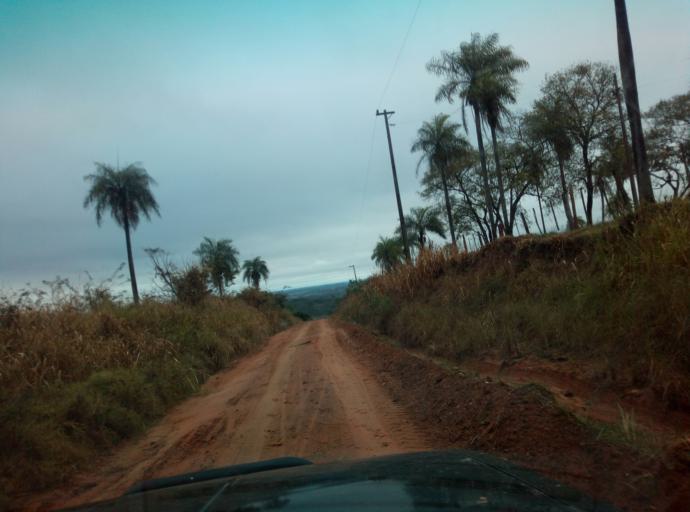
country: PY
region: Caaguazu
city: Carayao
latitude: -25.1903
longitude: -56.3657
